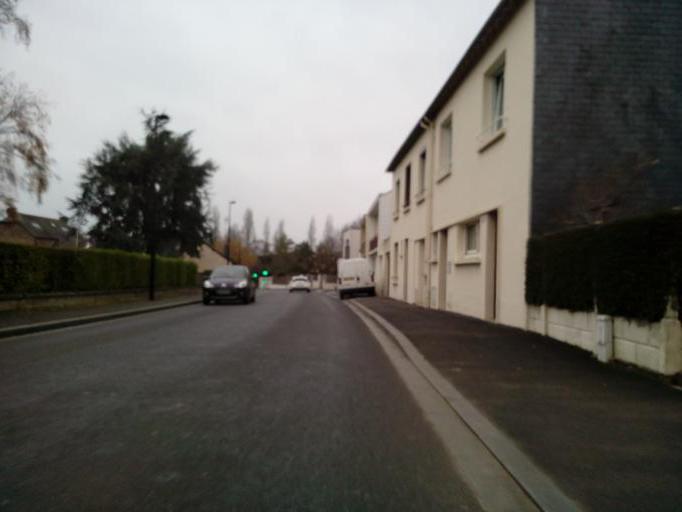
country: FR
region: Brittany
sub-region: Departement d'Ille-et-Vilaine
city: Saint-Jacques-de-la-Lande
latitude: 48.0886
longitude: -1.6991
